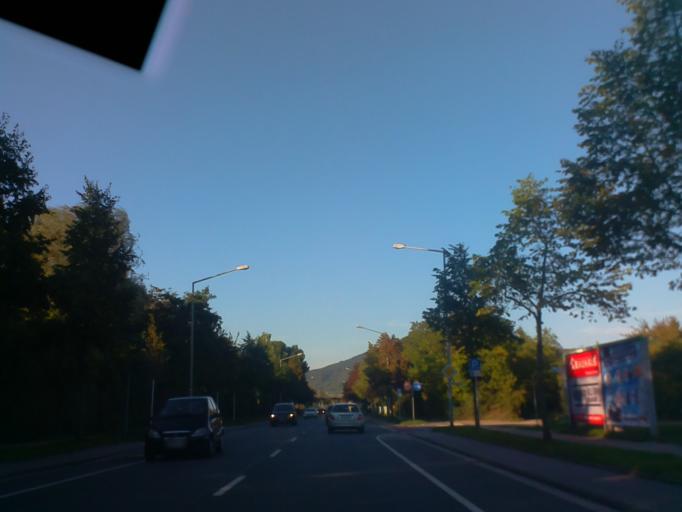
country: DE
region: Hesse
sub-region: Regierungsbezirk Darmstadt
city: Bensheim
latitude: 49.6845
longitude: 8.6050
